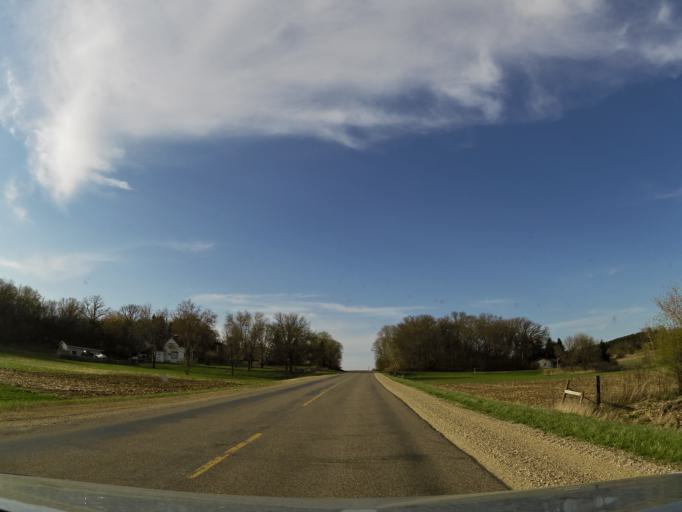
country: US
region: Wisconsin
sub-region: Pierce County
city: River Falls
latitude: 44.7539
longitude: -92.6396
